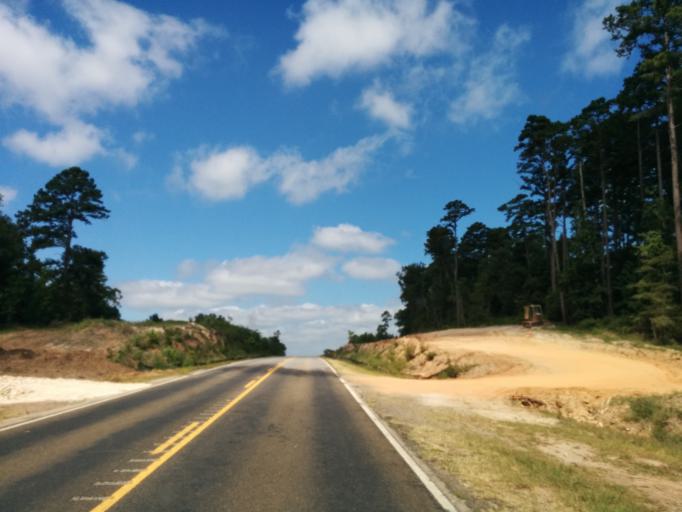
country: US
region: Texas
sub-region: Houston County
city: Hickory Creek
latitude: 31.3575
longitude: -95.2024
